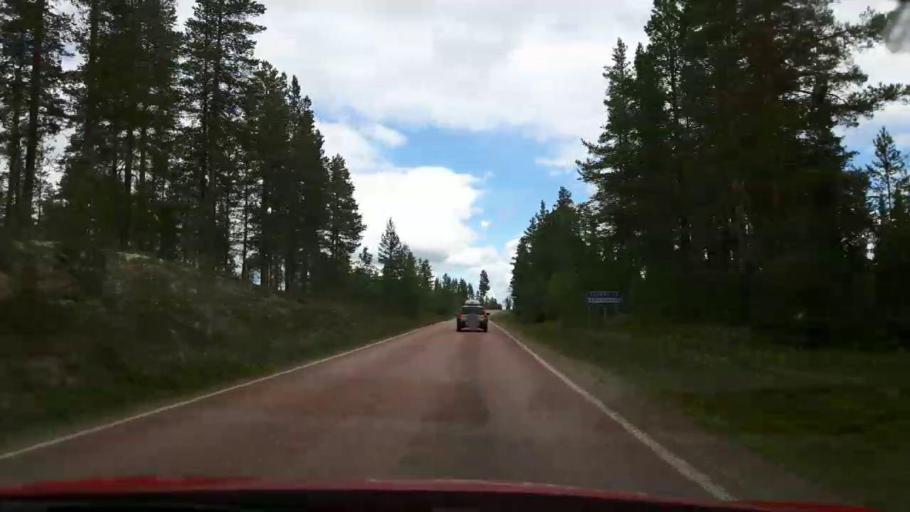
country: NO
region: Hedmark
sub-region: Trysil
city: Innbygda
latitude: 61.8668
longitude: 12.9551
